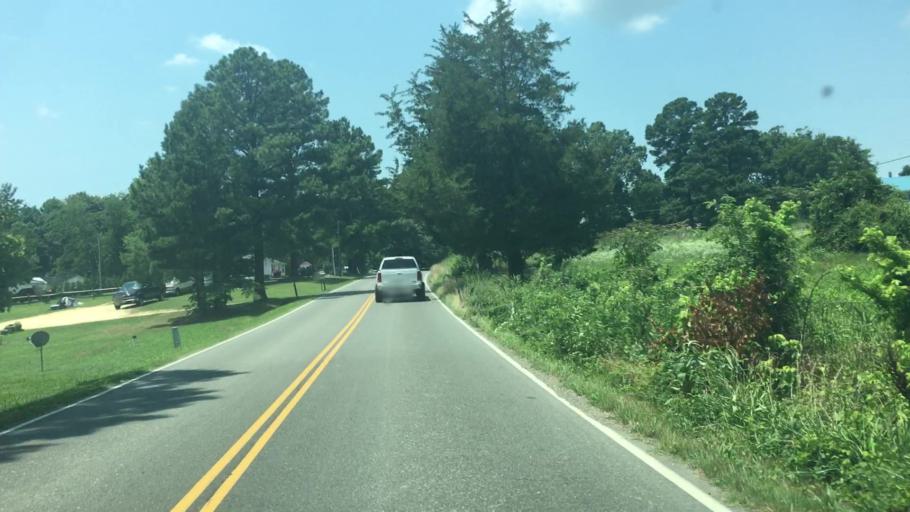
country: US
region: Maryland
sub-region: Saint Mary's County
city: Leonardtown
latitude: 38.3734
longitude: -76.6808
